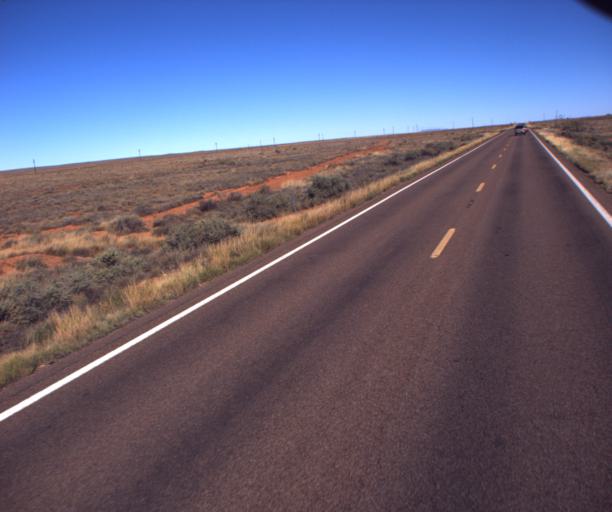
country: US
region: Arizona
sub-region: Navajo County
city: Holbrook
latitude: 34.7864
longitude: -110.1316
